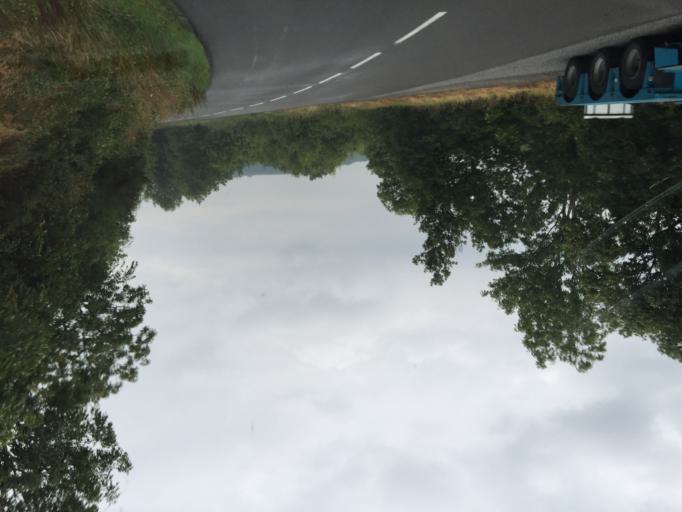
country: FR
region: Rhone-Alpes
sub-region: Departement de la Loire
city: Saint-Christo-en-Jarez
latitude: 45.5326
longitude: 4.4907
